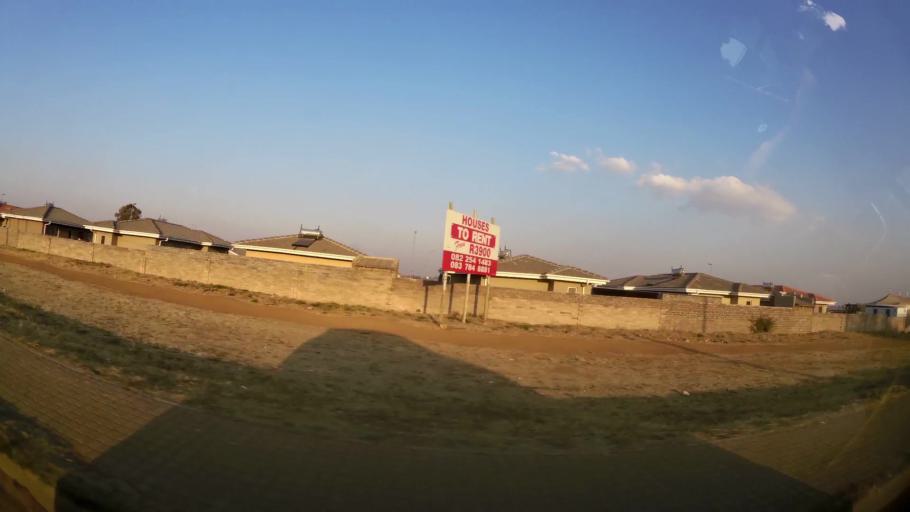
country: ZA
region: Gauteng
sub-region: Ekurhuleni Metropolitan Municipality
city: Benoni
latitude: -26.1558
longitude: 28.3775
